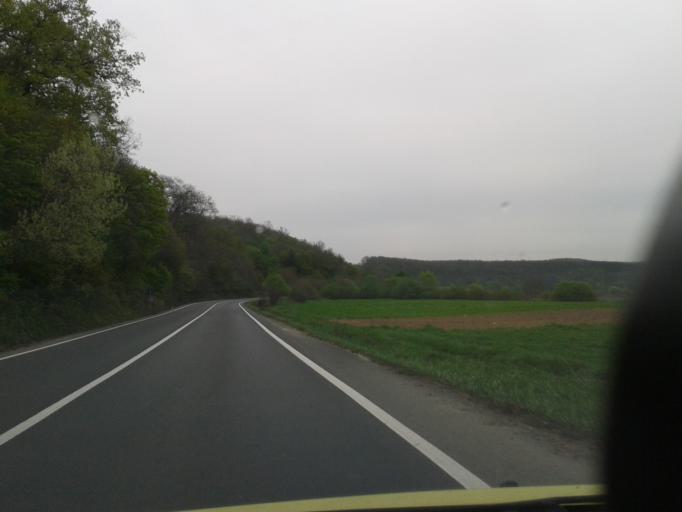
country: RO
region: Arad
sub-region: Comuna Ususau
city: Ususau
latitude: 46.1067
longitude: 21.7750
